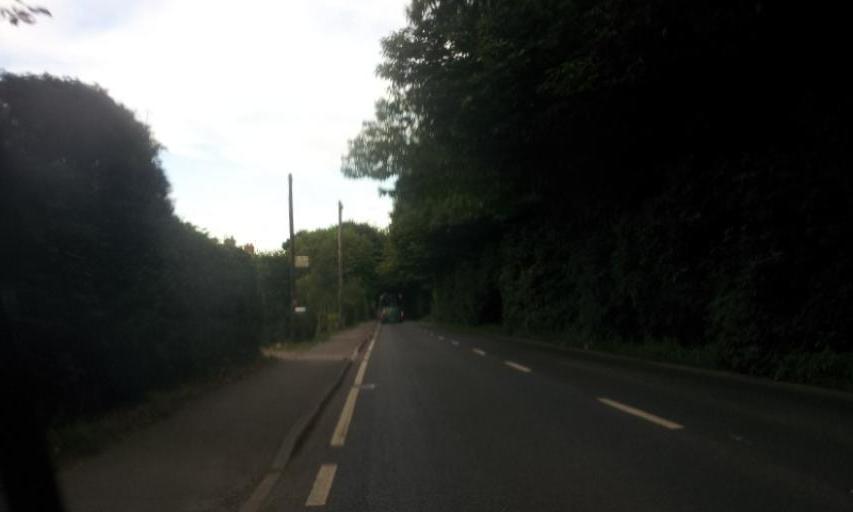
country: GB
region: England
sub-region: Kent
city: Maidstone
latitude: 51.2294
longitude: 0.5282
